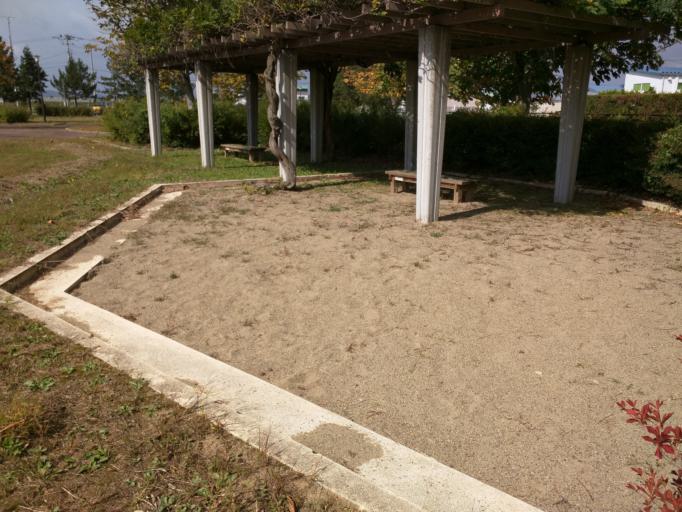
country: JP
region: Fukushima
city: Kitakata
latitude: 37.5252
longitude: 139.8697
